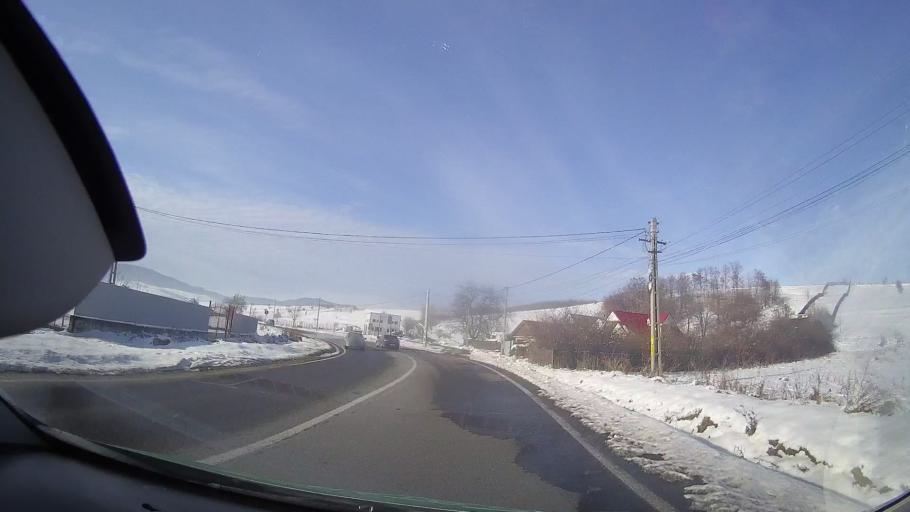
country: RO
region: Neamt
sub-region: Comuna Dobreni
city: Dobreni
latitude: 46.9979
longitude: 26.3884
